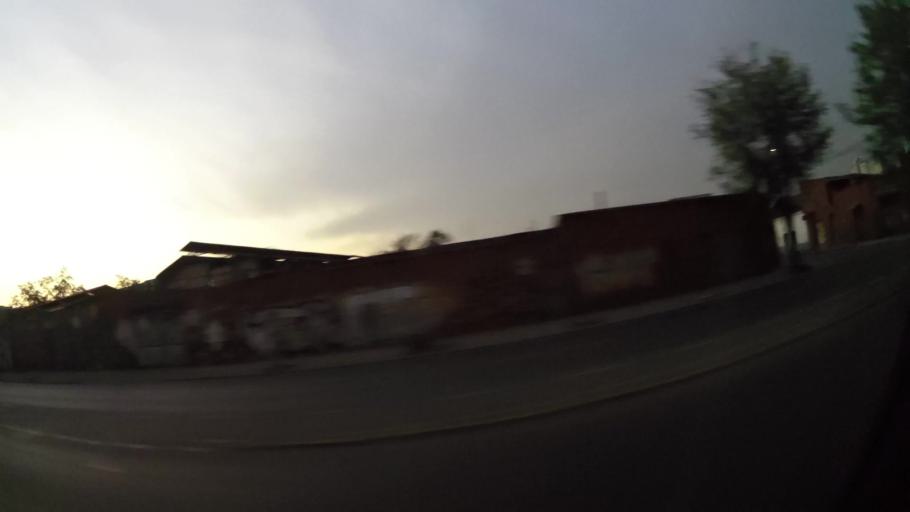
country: CL
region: Santiago Metropolitan
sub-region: Provincia de Santiago
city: Lo Prado
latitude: -33.4602
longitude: -70.6949
